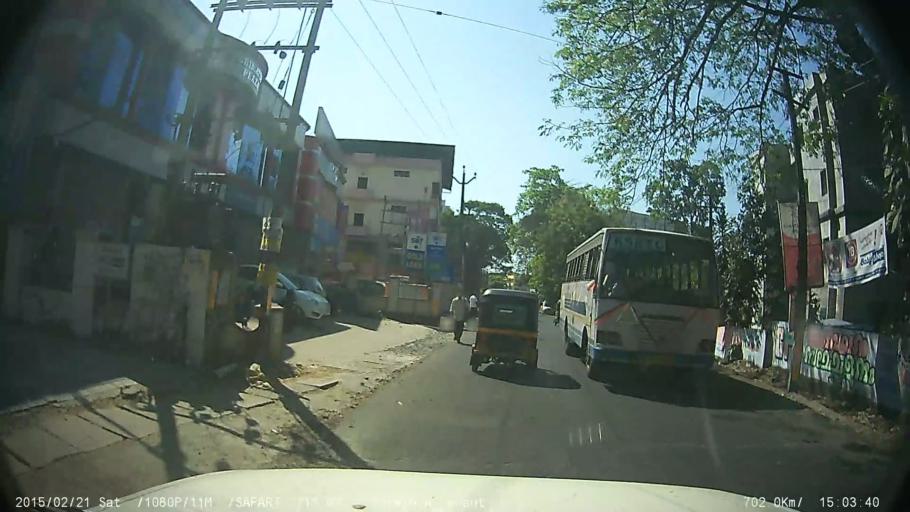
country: IN
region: Kerala
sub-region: Kottayam
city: Kottayam
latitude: 9.5948
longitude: 76.5301
